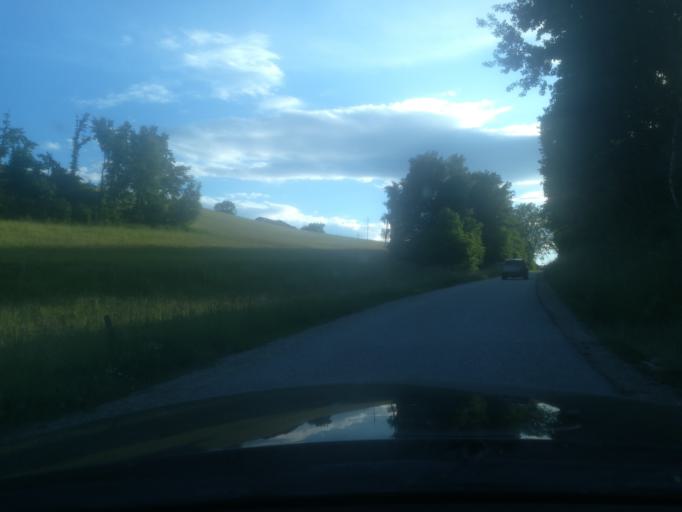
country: AT
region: Upper Austria
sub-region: Politischer Bezirk Perg
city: Perg
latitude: 48.3067
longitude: 14.6071
